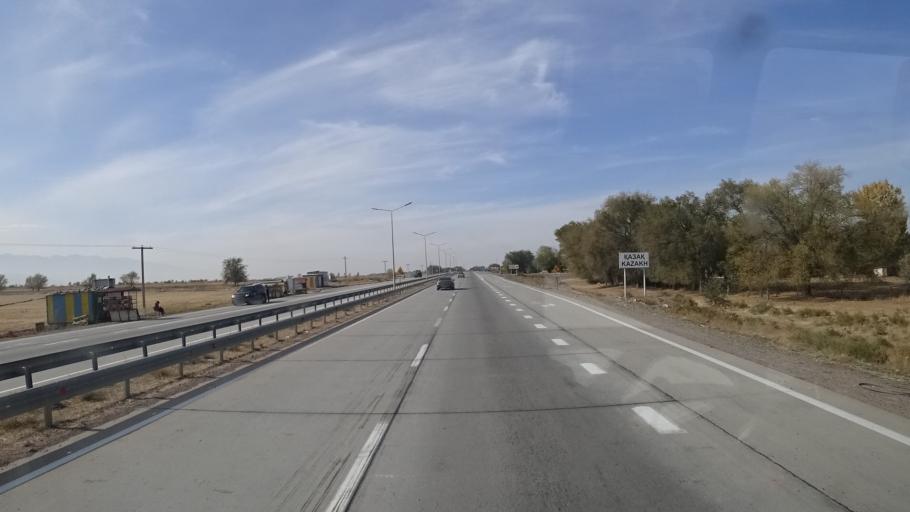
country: KZ
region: Zhambyl
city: Lugovoy
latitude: 42.9056
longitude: 72.9138
